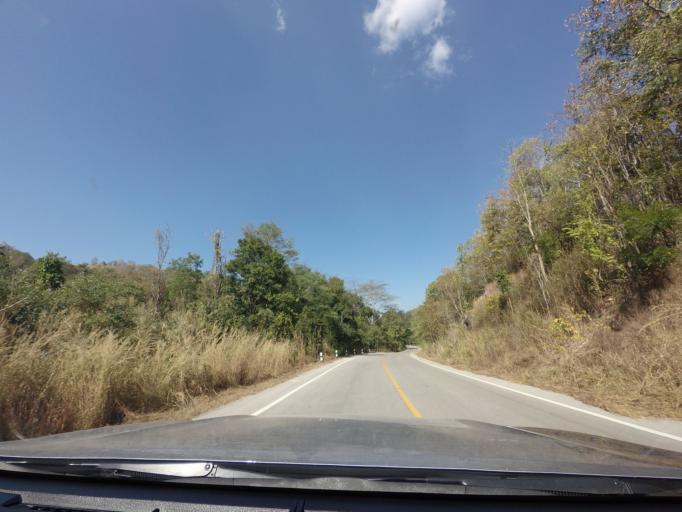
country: TH
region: Lampang
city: Chae Hom
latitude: 18.5787
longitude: 99.6270
